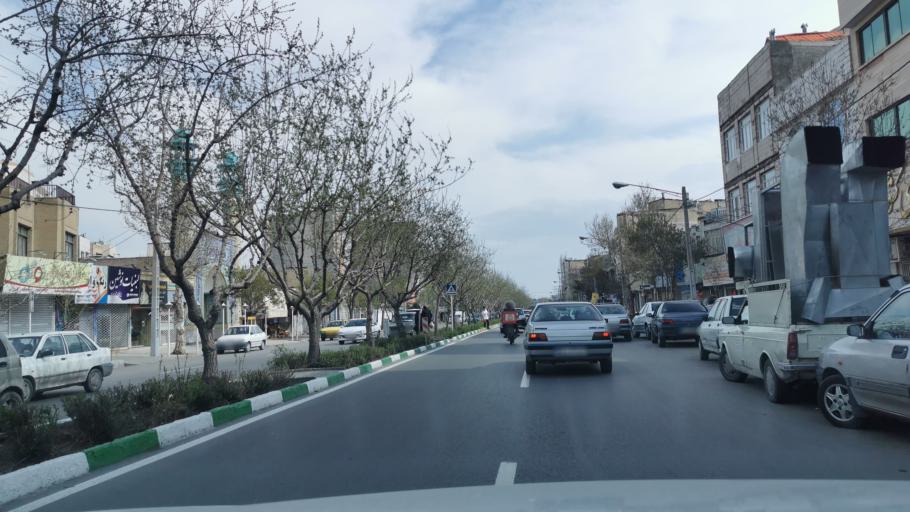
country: IR
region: Razavi Khorasan
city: Mashhad
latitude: 36.3143
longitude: 59.6115
